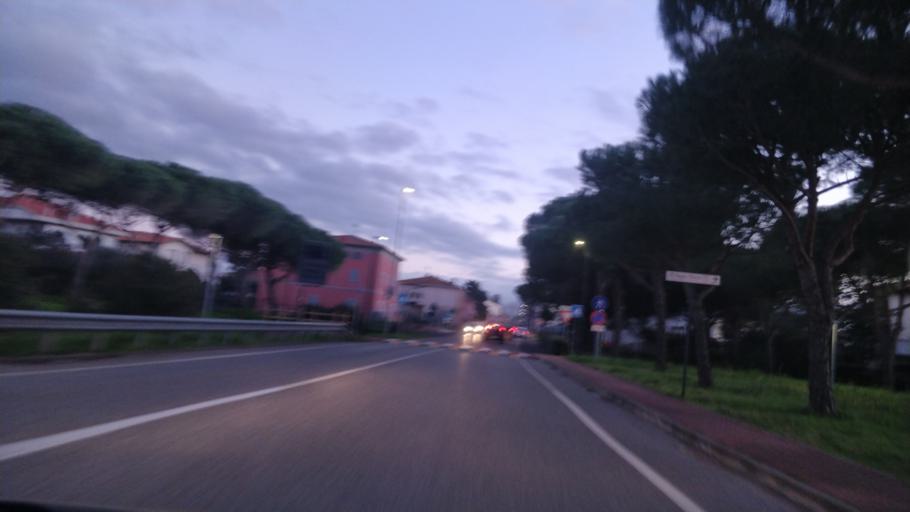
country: IT
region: Tuscany
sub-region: Provincia di Livorno
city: Vada
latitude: 43.3549
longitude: 10.4555
